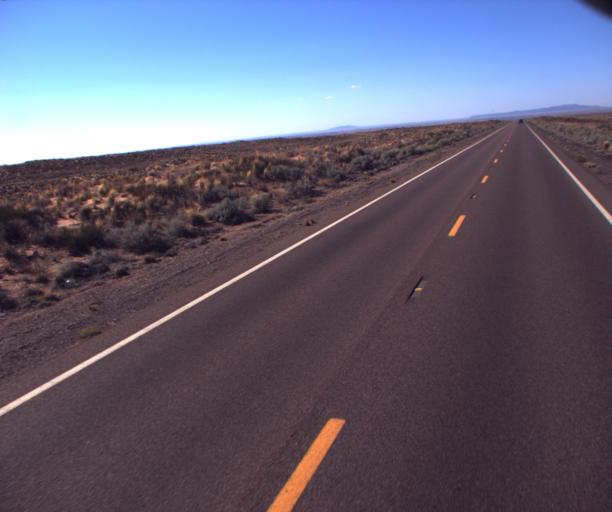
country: US
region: Arizona
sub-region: Navajo County
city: Winslow
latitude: 35.0579
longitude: -110.5879
